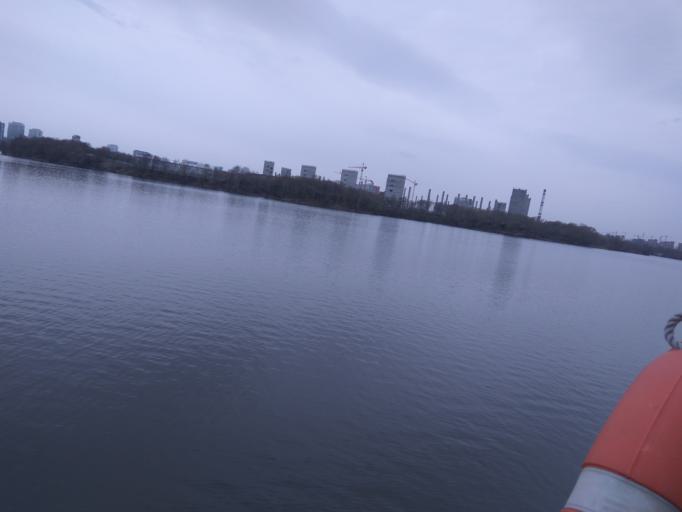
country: RU
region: Moskovskaya
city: Kozhukhovo
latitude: 55.6960
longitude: 37.6897
